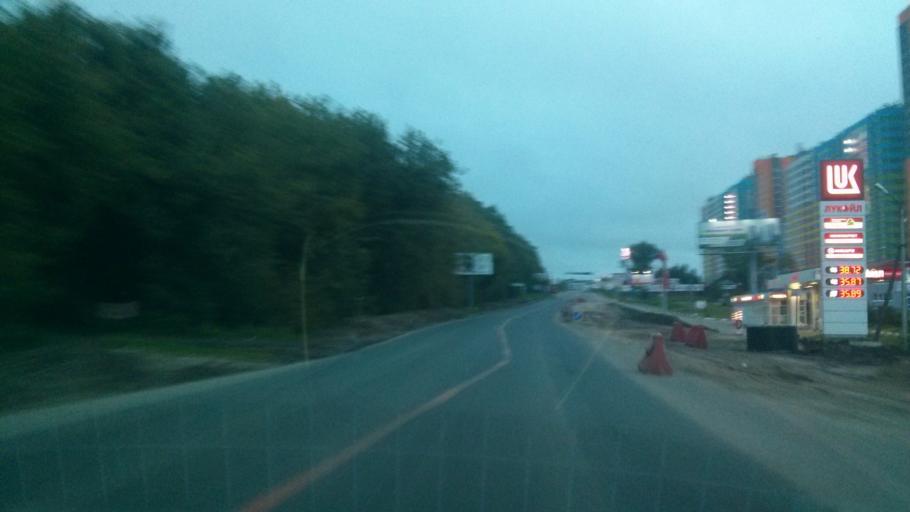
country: RU
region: Nizjnij Novgorod
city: Afonino
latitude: 56.2739
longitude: 44.0843
